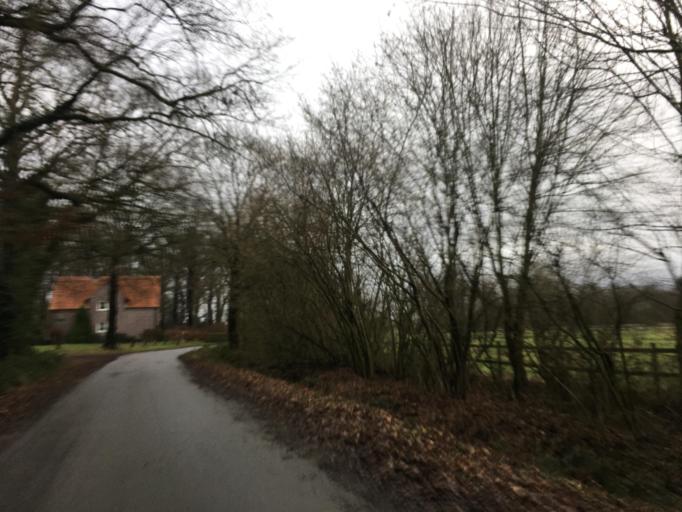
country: DE
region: North Rhine-Westphalia
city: Olfen
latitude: 51.7708
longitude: 7.3743
